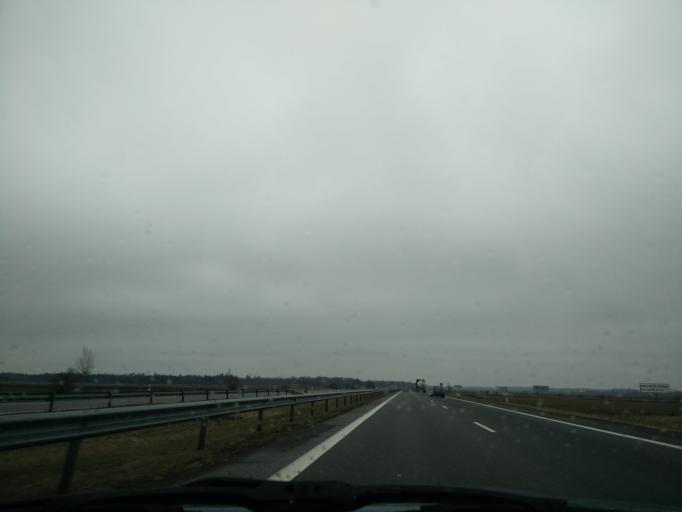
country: LT
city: Raseiniai
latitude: 55.3686
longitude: 22.9745
